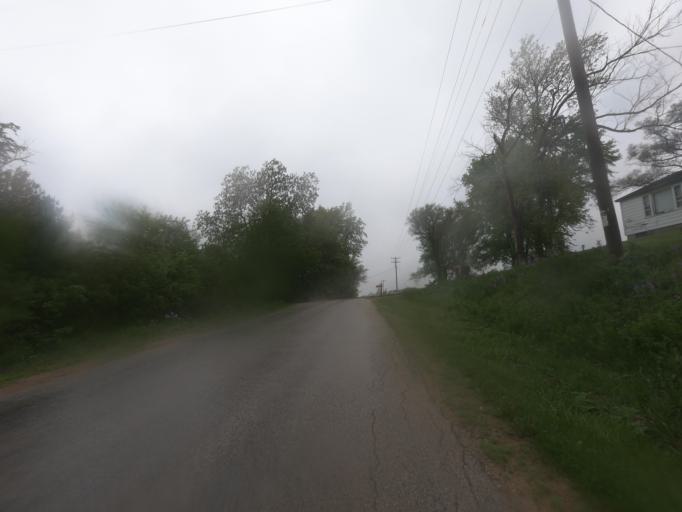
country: US
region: Wisconsin
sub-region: Grant County
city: Hazel Green
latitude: 42.5095
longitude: -90.4618
